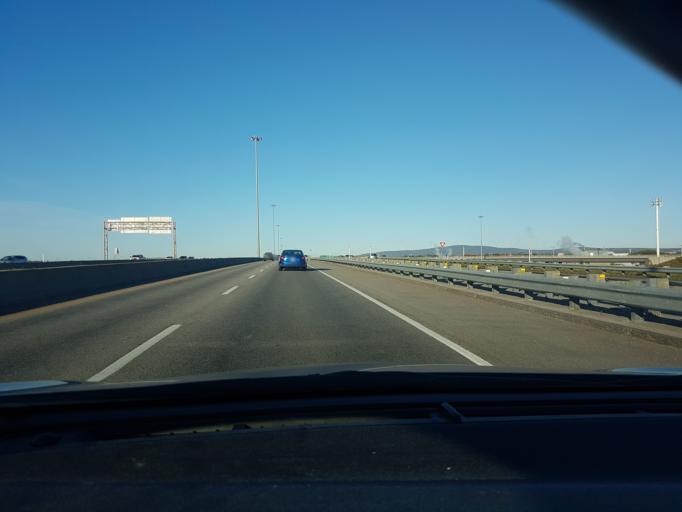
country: CA
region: Quebec
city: L'Ancienne-Lorette
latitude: 46.7946
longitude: -71.2860
